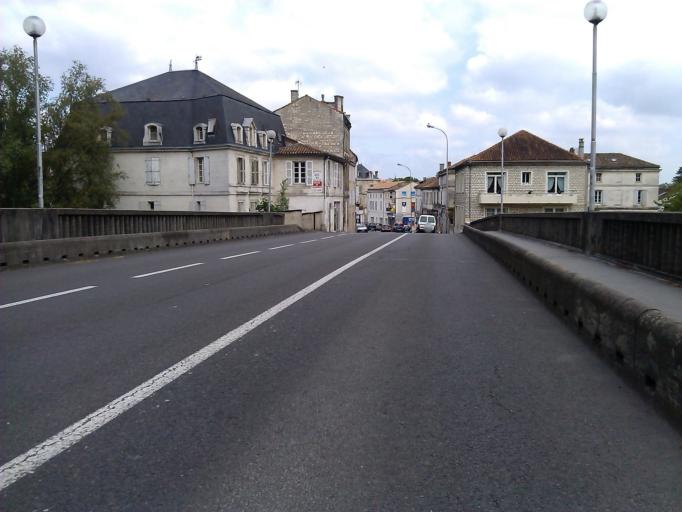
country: FR
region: Poitou-Charentes
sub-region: Departement de la Charente
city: Angouleme
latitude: 45.6547
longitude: 0.1483
